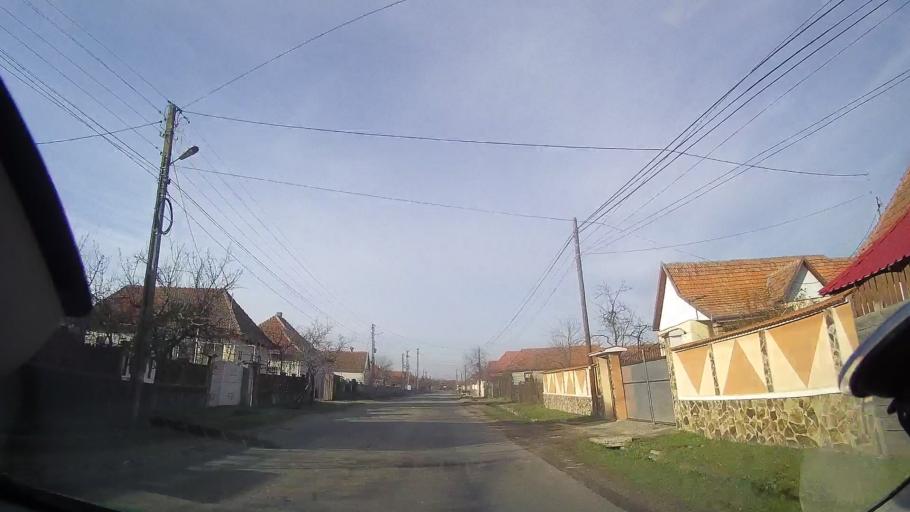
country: RO
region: Bihor
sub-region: Comuna Brusturi
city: Brusturi
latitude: 47.1527
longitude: 22.2469
